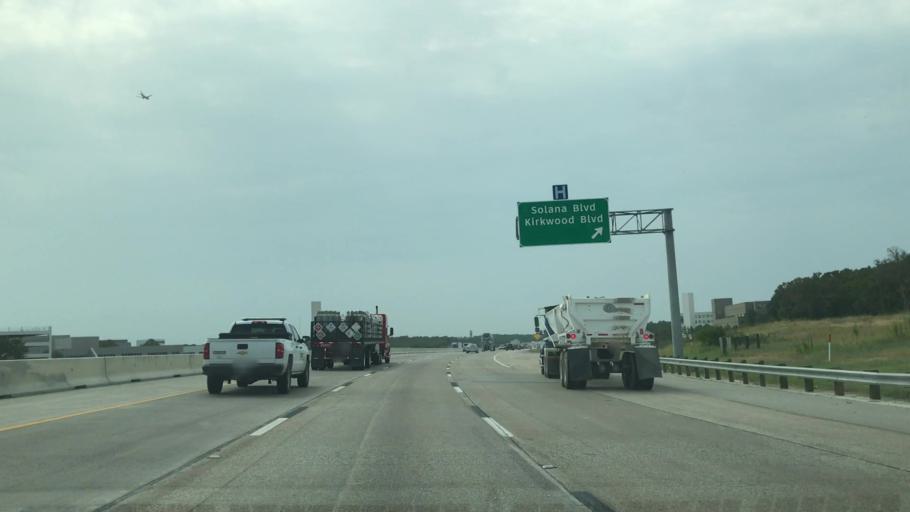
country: US
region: Texas
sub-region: Denton County
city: Trophy Club
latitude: 32.9852
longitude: -97.1704
